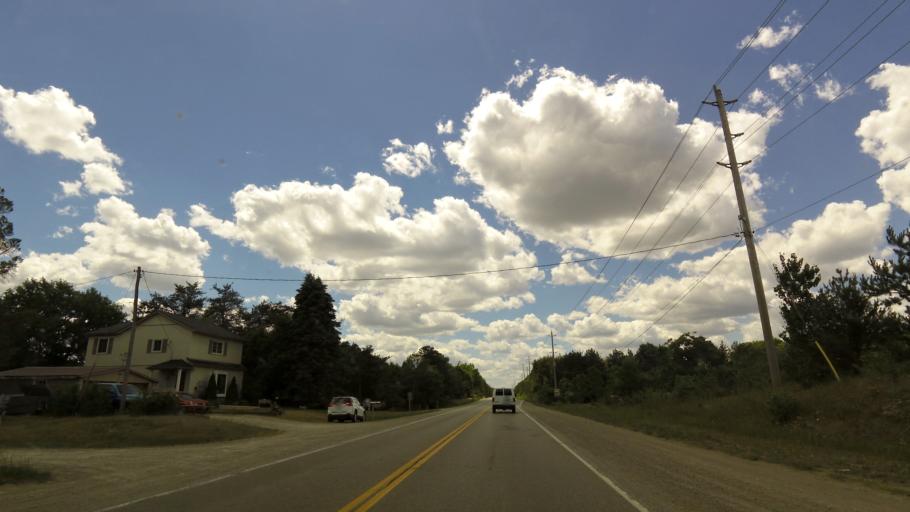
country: CA
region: Ontario
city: Uxbridge
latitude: 44.0431
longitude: -79.1578
